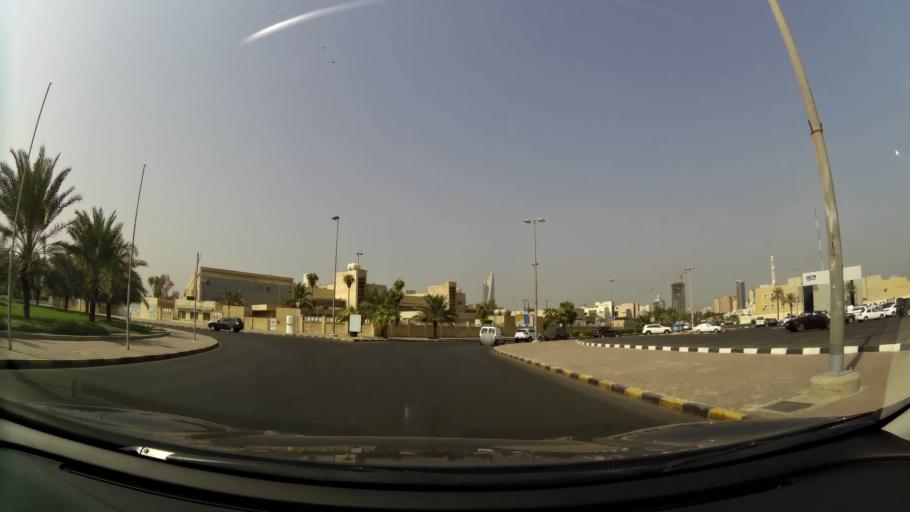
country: KW
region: Al Asimah
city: Ad Dasmah
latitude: 29.3572
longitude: 48.0122
